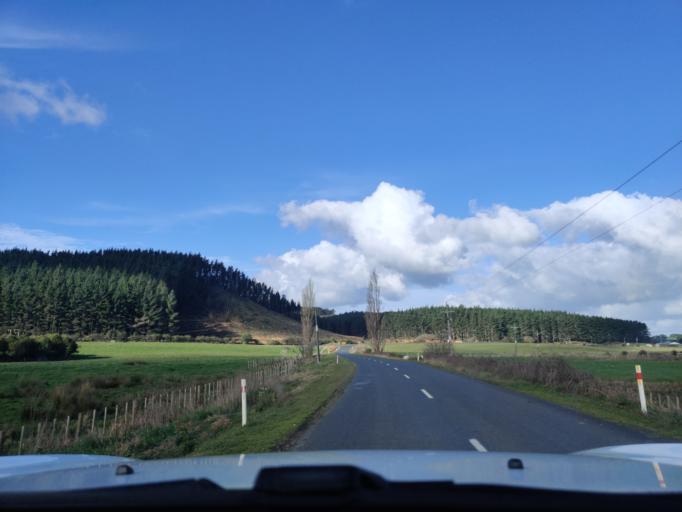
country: NZ
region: Waikato
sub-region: Waikato District
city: Te Kauwhata
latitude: -37.2916
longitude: 175.2237
